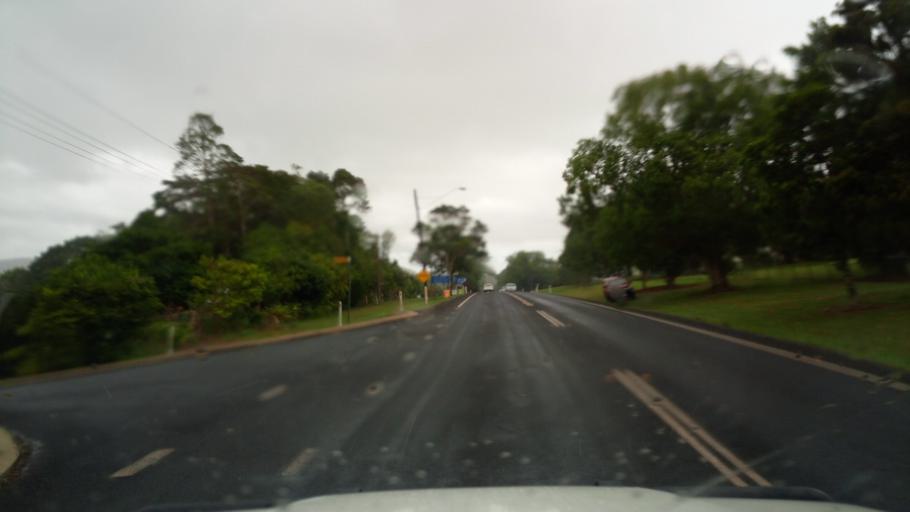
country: AU
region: Queensland
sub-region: Tablelands
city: Tolga
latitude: -17.2749
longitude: 145.5862
